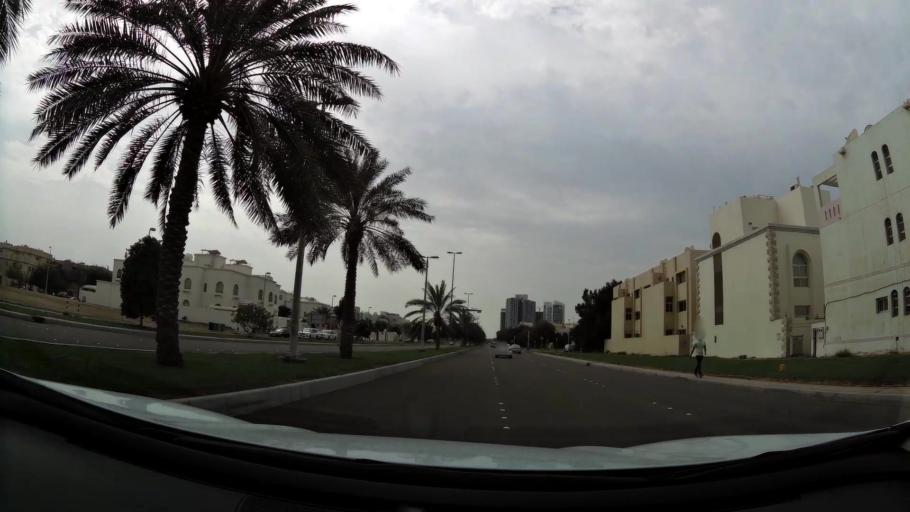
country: AE
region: Abu Dhabi
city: Abu Dhabi
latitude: 24.4393
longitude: 54.4395
